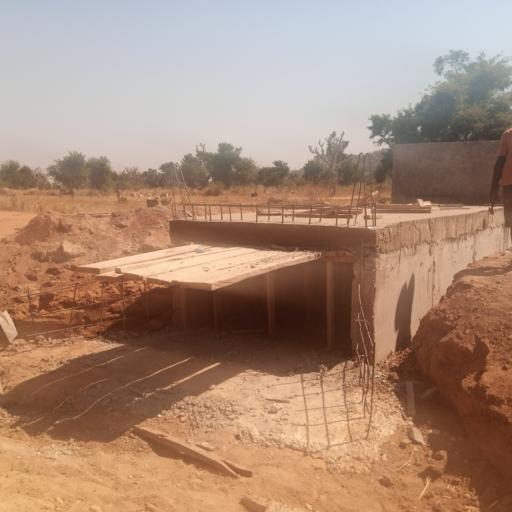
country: NG
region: Adamawa
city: Yola
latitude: 9.1201
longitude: 12.3962
